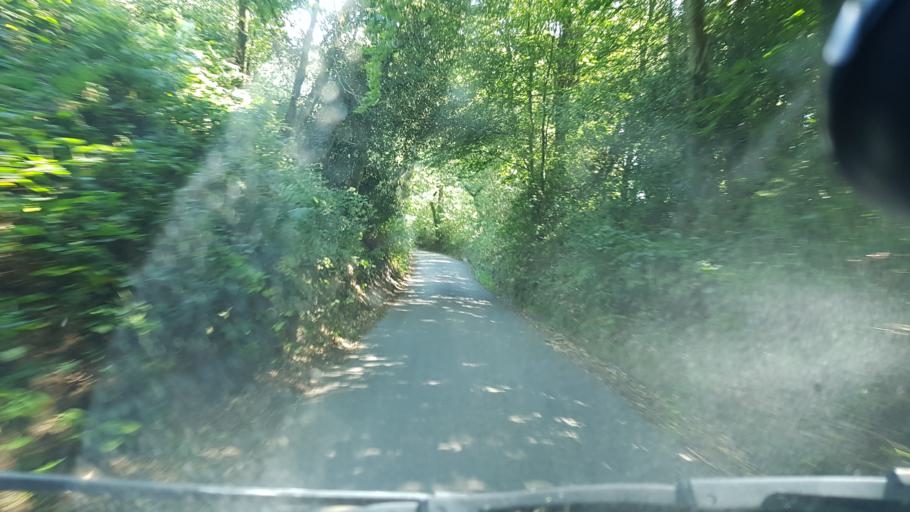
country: GB
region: England
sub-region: Surrey
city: Cranleigh
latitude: 51.1728
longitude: -0.4878
